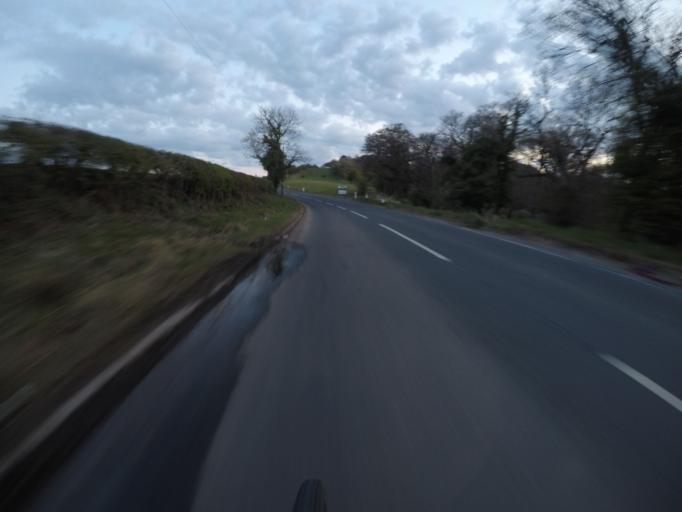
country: GB
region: Scotland
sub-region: South Ayrshire
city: Dundonald
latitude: 55.5686
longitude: -4.5999
